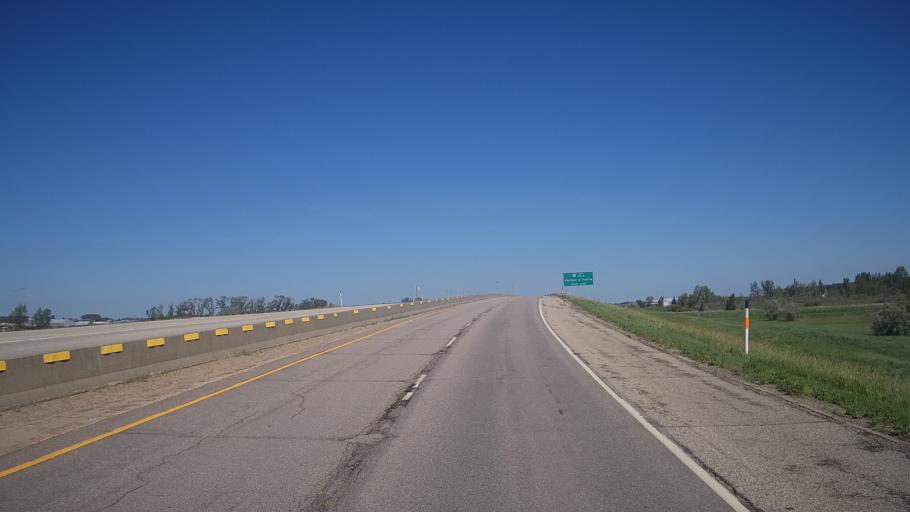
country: CA
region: Manitoba
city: Portage la Prairie
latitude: 49.9653
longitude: -98.3556
